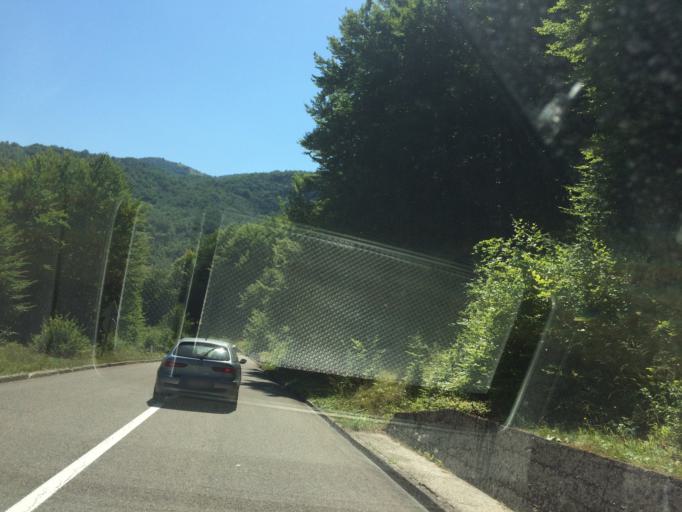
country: ME
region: Opstina Savnik
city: Savnik
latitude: 42.9524
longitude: 19.0959
